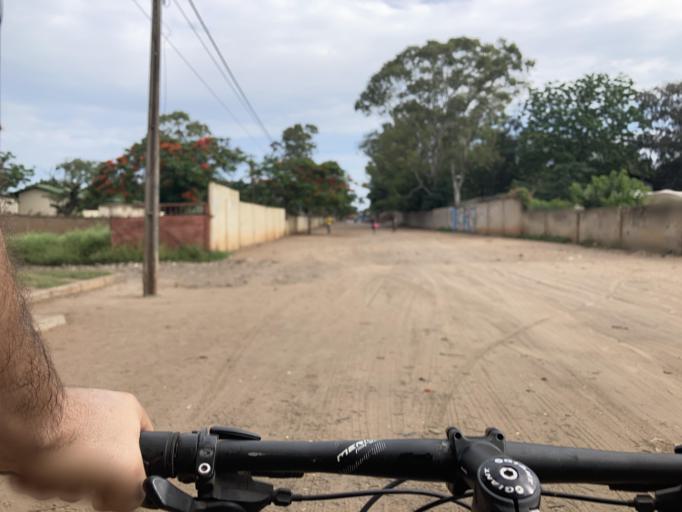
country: MZ
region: Maputo City
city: Maputo
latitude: -25.9302
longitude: 32.5842
